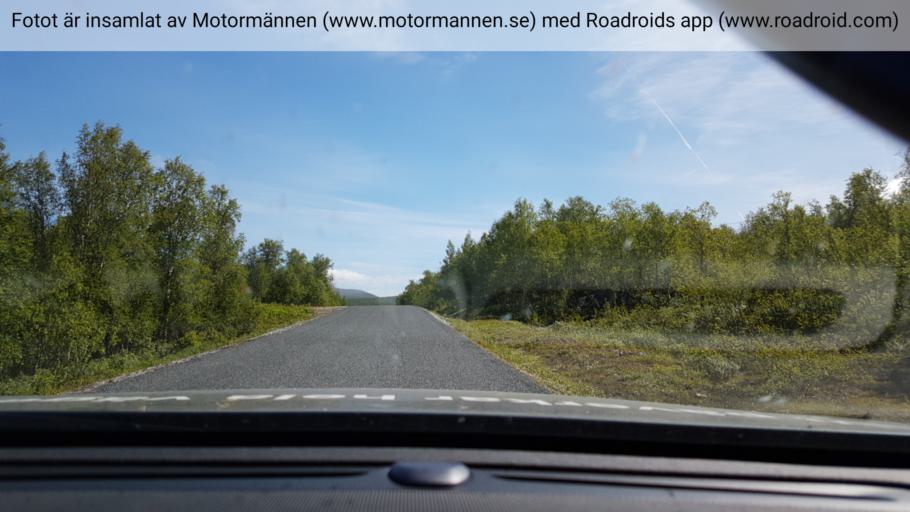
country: NO
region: Nordland
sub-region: Hattfjelldal
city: Hattfjelldal
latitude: 65.4239
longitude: 14.8918
